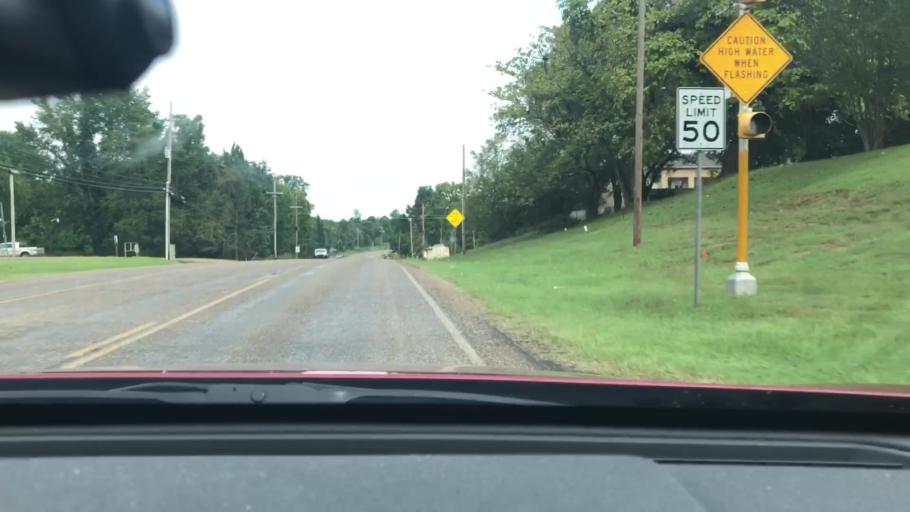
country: US
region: Texas
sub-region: Bowie County
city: Wake Village
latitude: 33.4431
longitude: -94.1106
